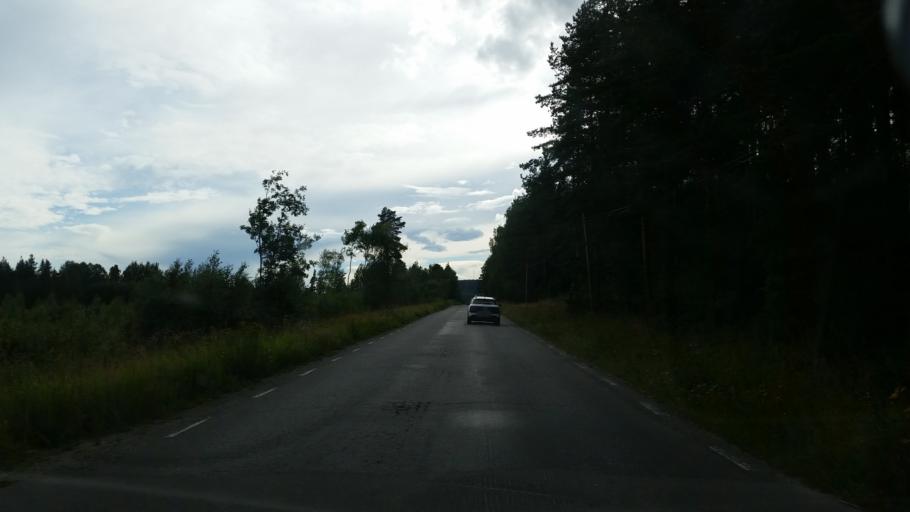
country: SE
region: Gaevleborg
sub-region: Hudiksvalls Kommun
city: Delsbo
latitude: 61.9087
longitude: 16.5694
